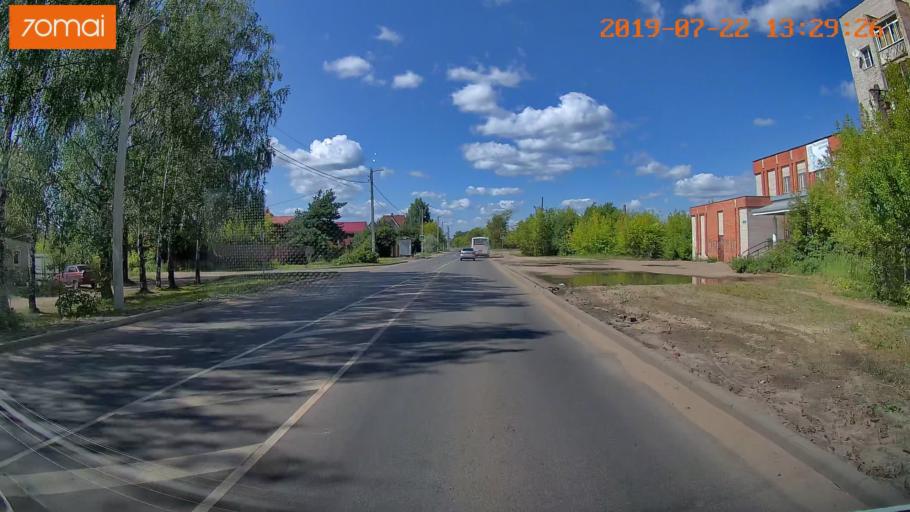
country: RU
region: Ivanovo
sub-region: Gorod Ivanovo
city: Ivanovo
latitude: 57.0473
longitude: 40.9386
